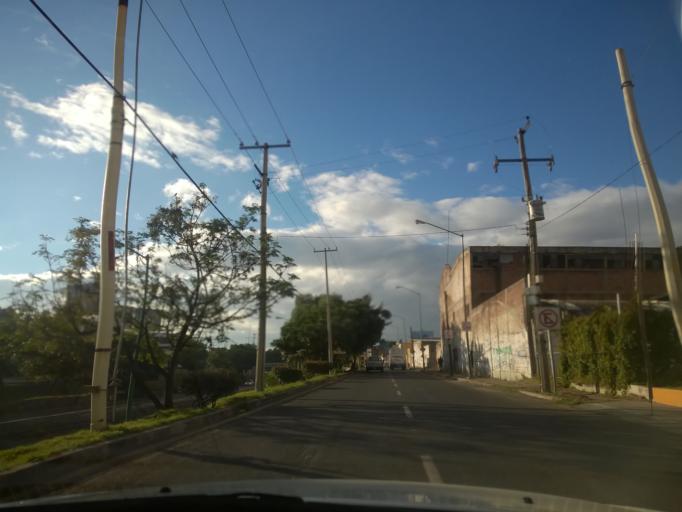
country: MX
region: Guanajuato
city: Leon
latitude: 21.1346
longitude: -101.6789
